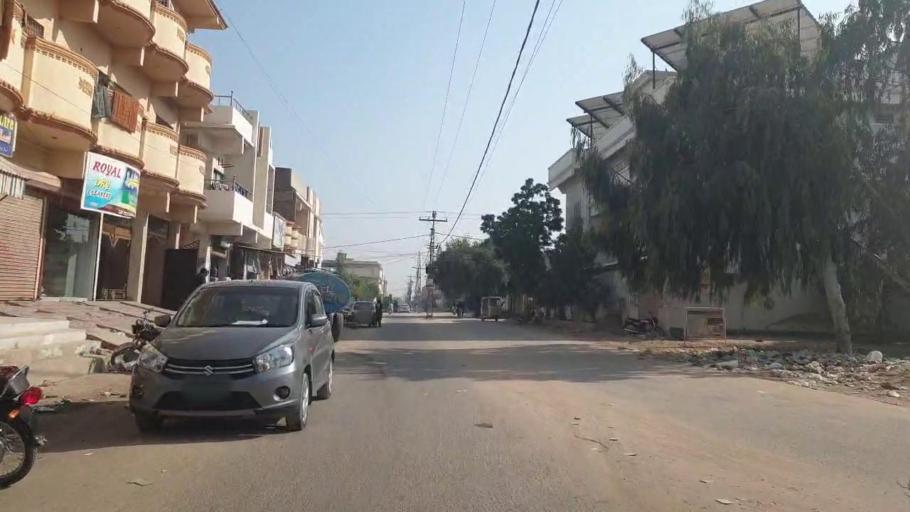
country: PK
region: Sindh
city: Jamshoro
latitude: 25.4128
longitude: 68.2742
